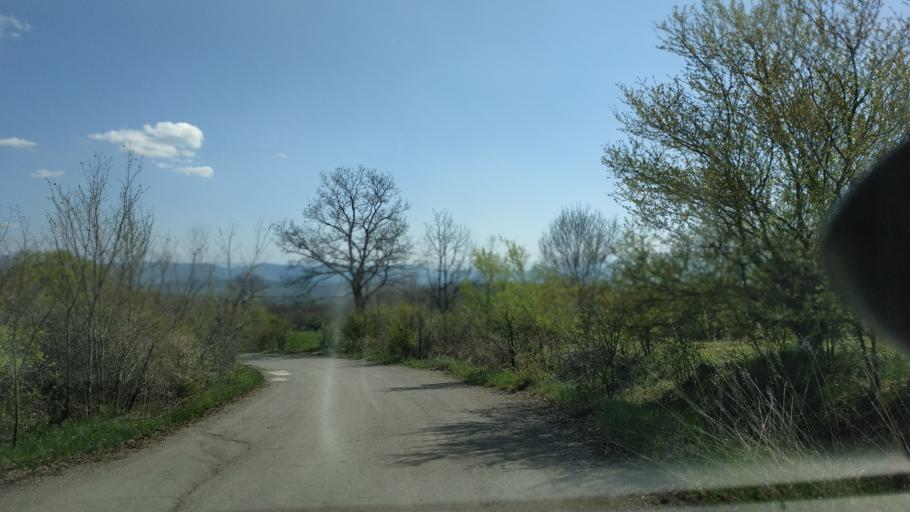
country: RS
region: Central Serbia
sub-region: Zajecarski Okrug
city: Soko Banja
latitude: 43.5517
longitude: 21.8972
